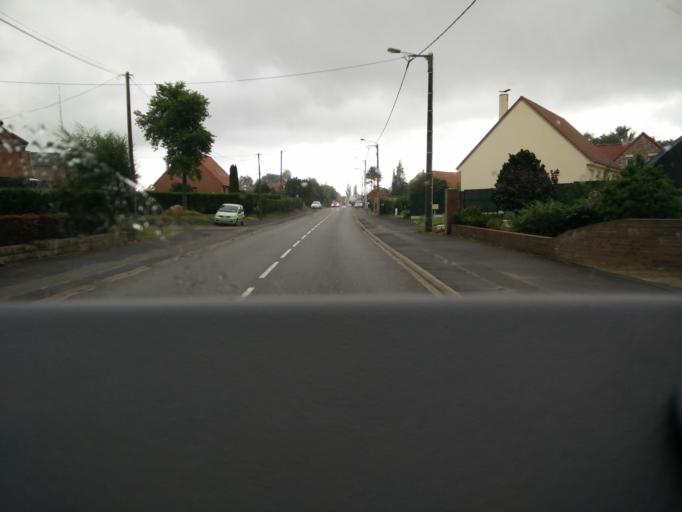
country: FR
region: Nord-Pas-de-Calais
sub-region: Departement du Pas-de-Calais
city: Bouvigny-Boyeffles
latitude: 50.4087
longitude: 2.6371
